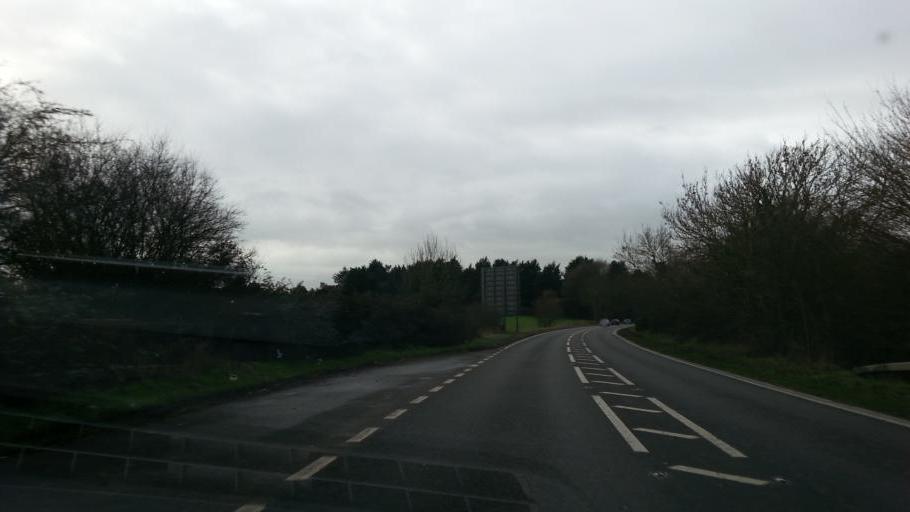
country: GB
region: England
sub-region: Cambridgeshire
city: Linton
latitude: 52.0931
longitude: 0.2922
